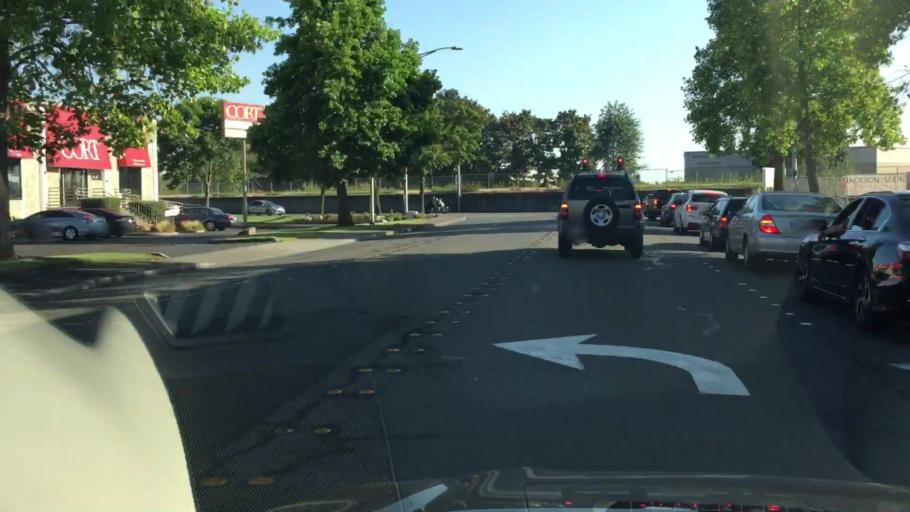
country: US
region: Washington
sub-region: King County
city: Tukwila
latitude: 47.4425
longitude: -122.2511
